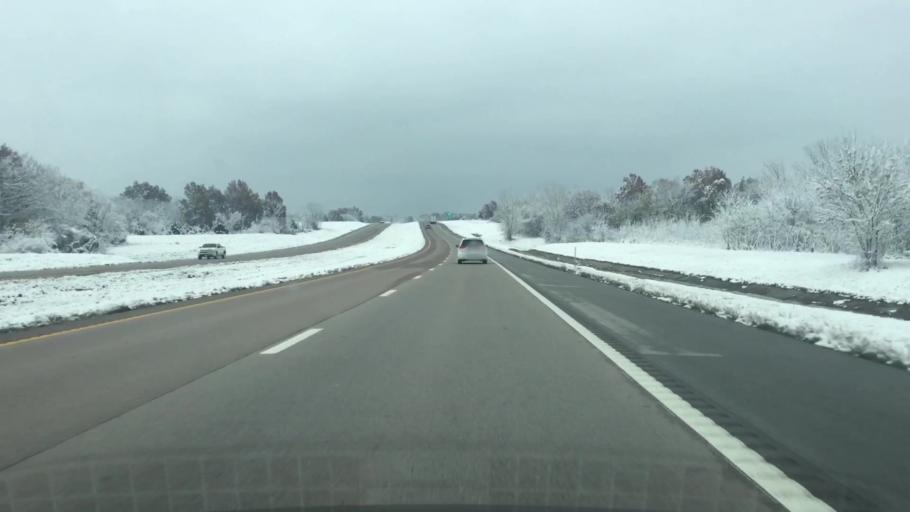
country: US
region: Missouri
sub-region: Cass County
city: Garden City
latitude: 38.4776
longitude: -94.0251
